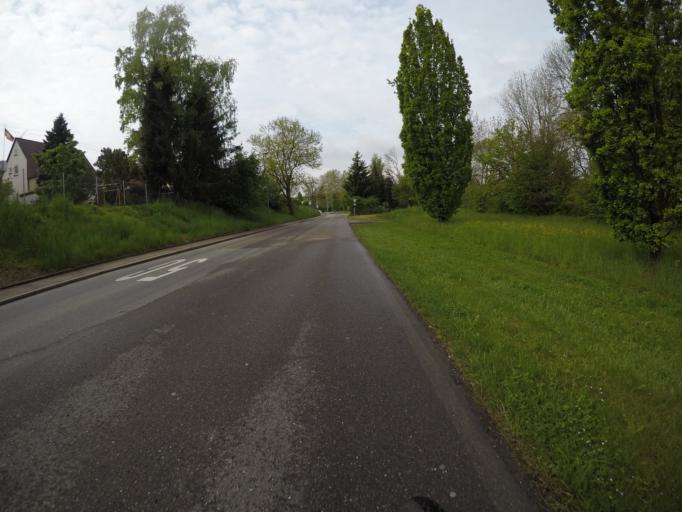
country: DE
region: Baden-Wuerttemberg
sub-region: Regierungsbezirk Stuttgart
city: Weil der Stadt
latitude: 48.7530
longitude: 8.8772
